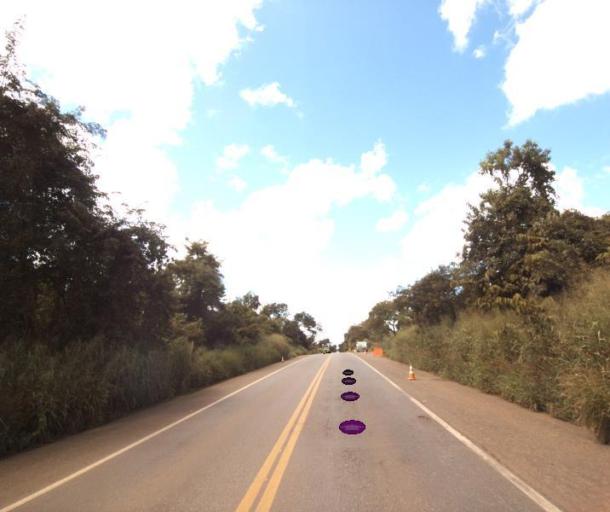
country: BR
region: Goias
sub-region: Petrolina De Goias
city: Petrolina de Goias
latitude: -16.0038
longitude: -49.1354
